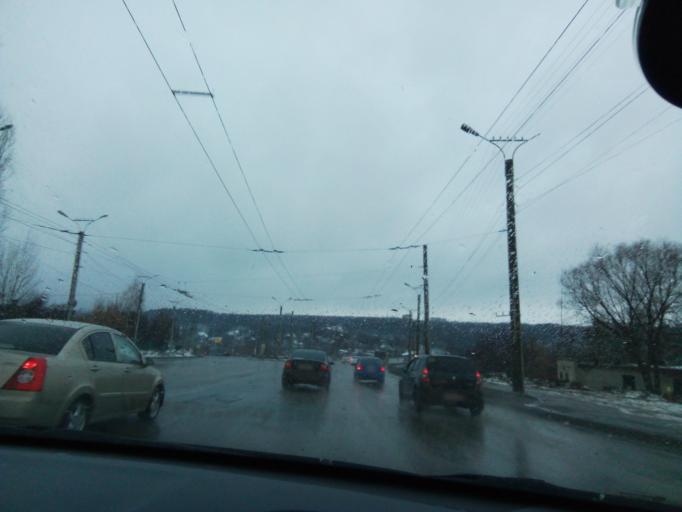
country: RU
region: Chuvashia
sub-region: Cheboksarskiy Rayon
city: Cheboksary
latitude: 56.1286
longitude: 47.2103
